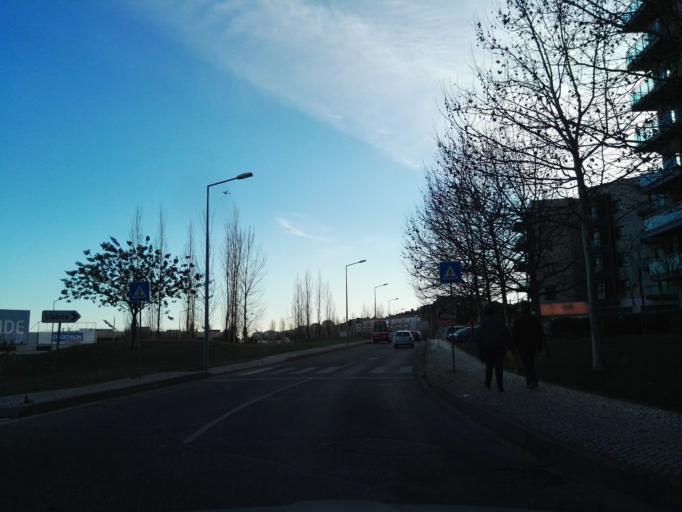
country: PT
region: Lisbon
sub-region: Vila Franca de Xira
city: Vialonga
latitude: 38.8871
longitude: -9.0462
